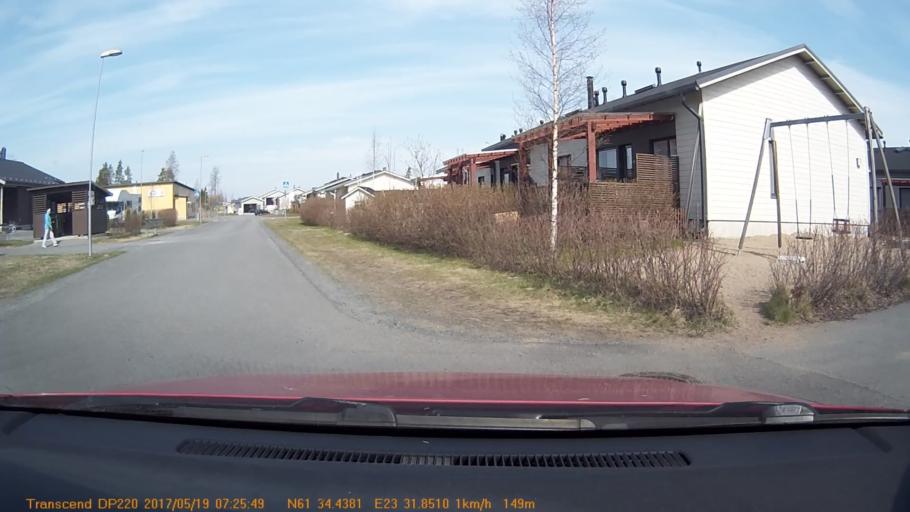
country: FI
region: Pirkanmaa
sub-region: Tampere
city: Yloejaervi
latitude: 61.5738
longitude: 23.5311
